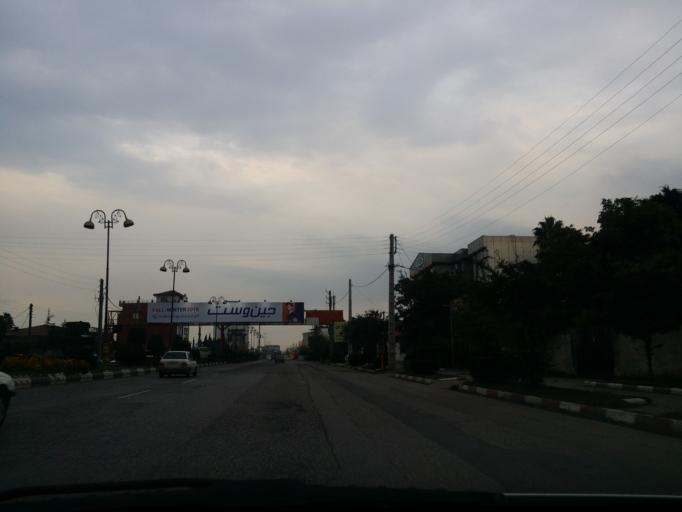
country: IR
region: Mazandaran
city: `Abbasabad
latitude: 36.7253
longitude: 51.1202
